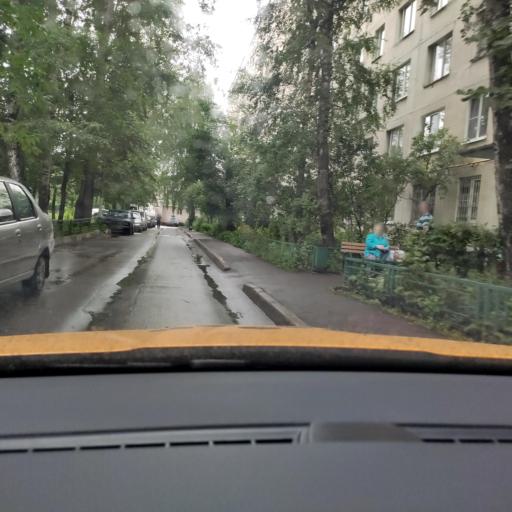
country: RU
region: Moskovskaya
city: Novogireyevo
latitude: 55.7515
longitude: 37.8333
